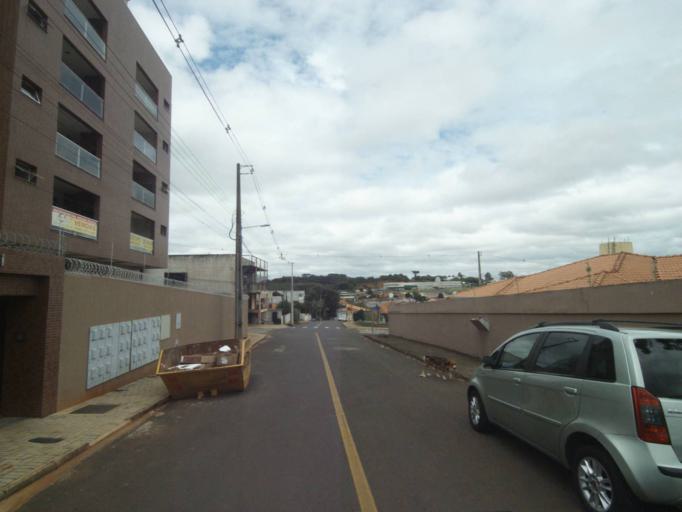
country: BR
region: Parana
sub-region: Telemaco Borba
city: Telemaco Borba
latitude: -24.3340
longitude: -50.6347
